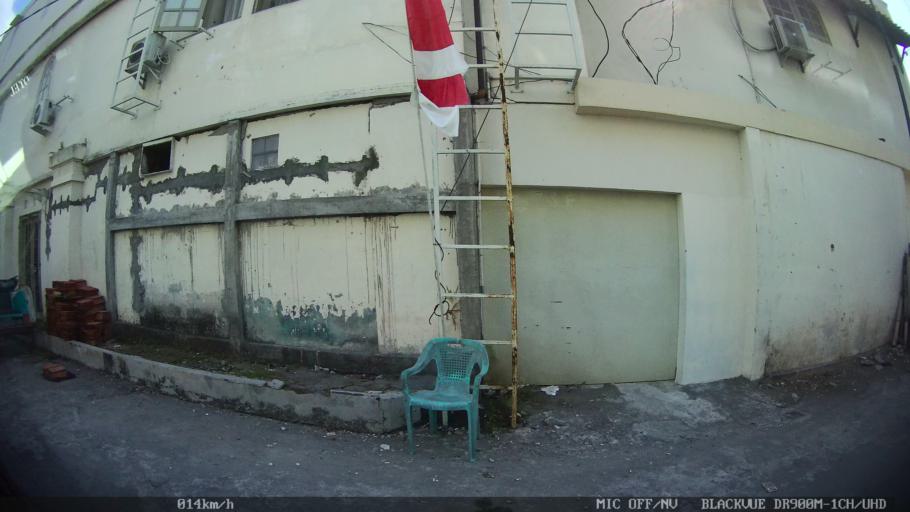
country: ID
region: Daerah Istimewa Yogyakarta
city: Yogyakarta
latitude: -7.8201
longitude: 110.3713
